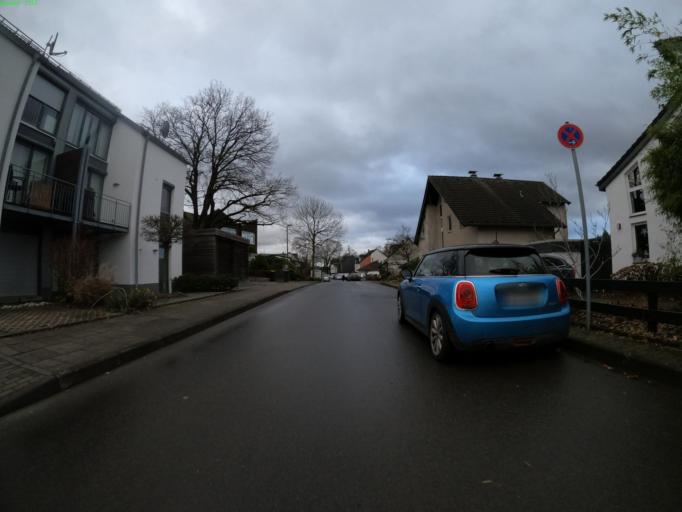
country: DE
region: North Rhine-Westphalia
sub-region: Regierungsbezirk Dusseldorf
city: Solingen
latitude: 51.1814
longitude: 7.1375
